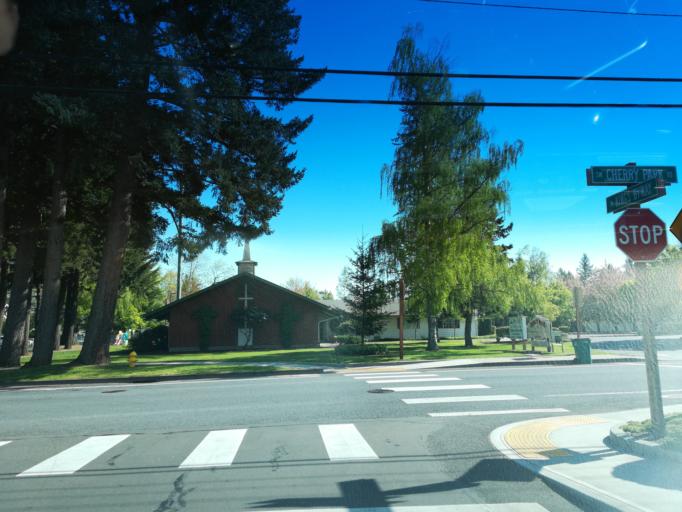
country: US
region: Oregon
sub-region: Multnomah County
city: Troutdale
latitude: 45.5338
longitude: -122.3918
